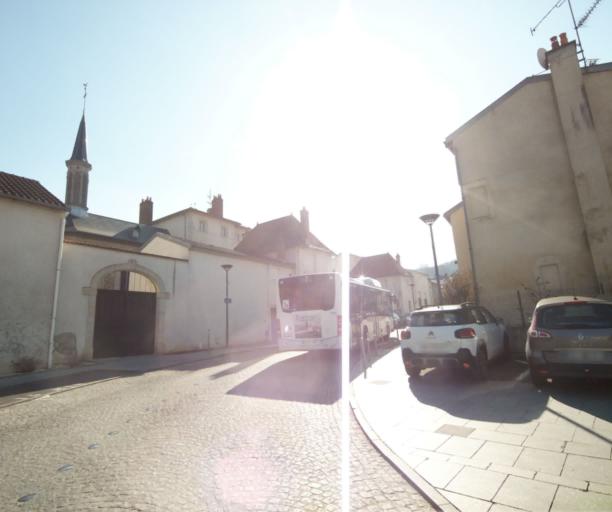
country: FR
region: Lorraine
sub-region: Departement de Meurthe-et-Moselle
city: Vandoeuvre-les-Nancy
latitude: 48.6463
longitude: 6.1756
